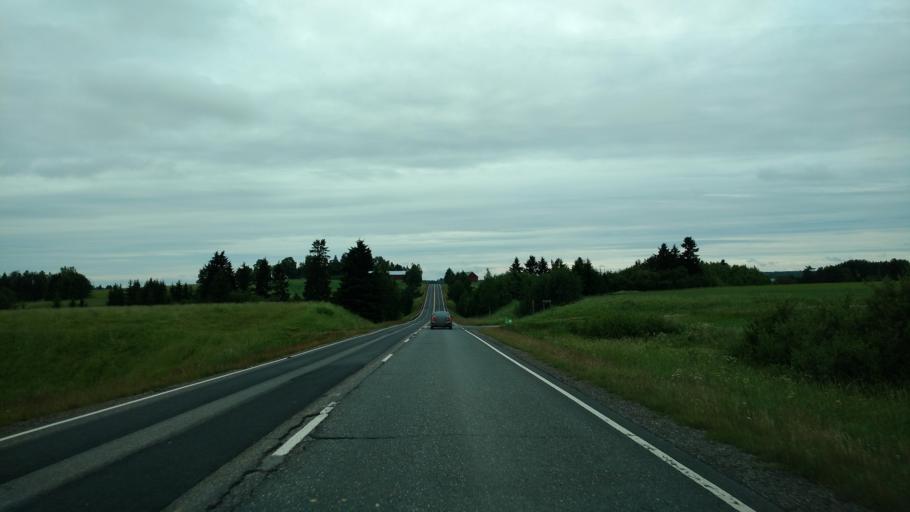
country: FI
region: Varsinais-Suomi
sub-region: Salo
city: Halikko
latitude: 60.4695
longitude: 23.0156
